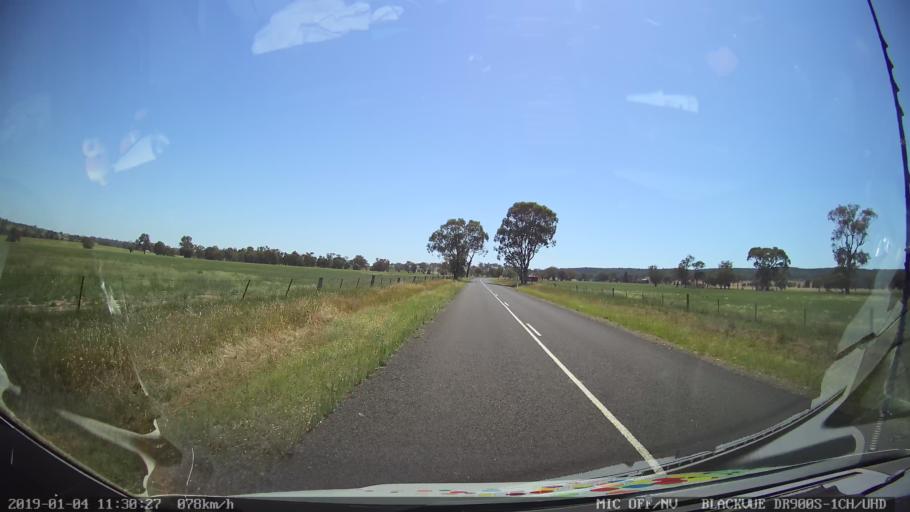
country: AU
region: New South Wales
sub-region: Cabonne
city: Molong
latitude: -33.0777
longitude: 148.7811
